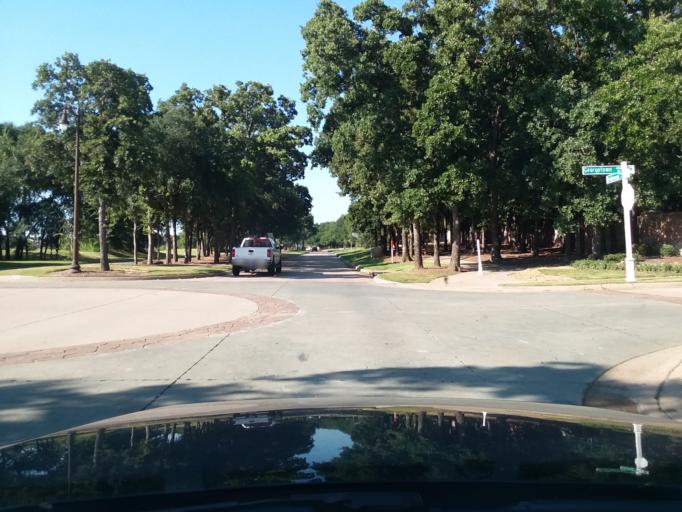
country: US
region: Texas
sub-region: Denton County
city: Double Oak
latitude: 33.0449
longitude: -97.0941
